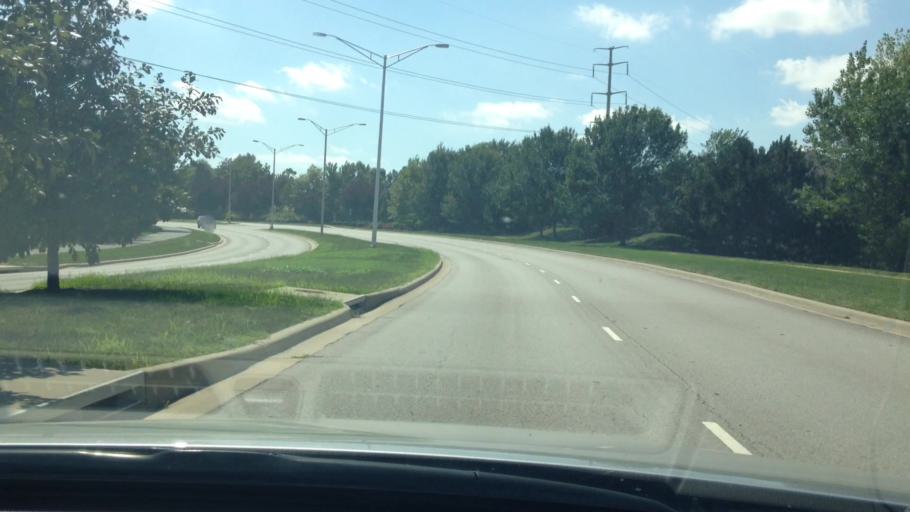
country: US
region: Kansas
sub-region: Johnson County
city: Lenexa
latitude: 38.8661
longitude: -94.7032
